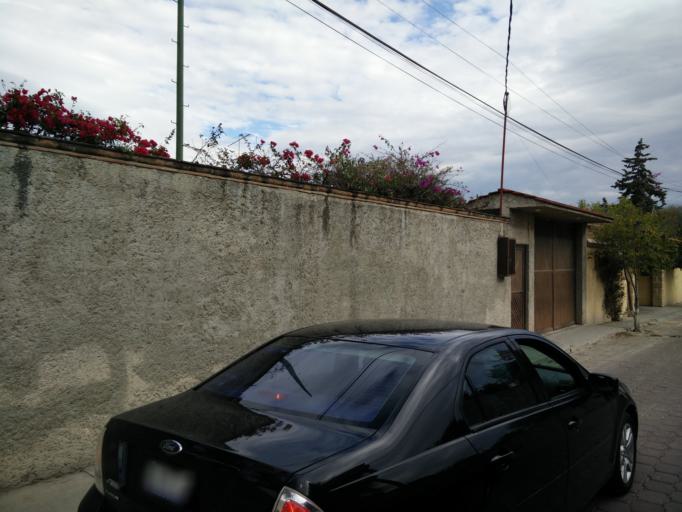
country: MX
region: Queretaro
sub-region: Tequisquiapan
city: Tequisquiapan
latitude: 20.5288
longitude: -99.8942
